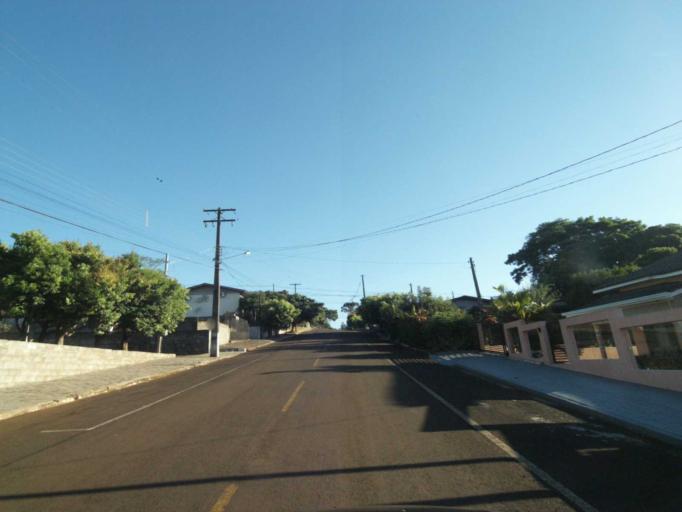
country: BR
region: Parana
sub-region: Coronel Vivida
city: Coronel Vivida
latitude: -25.9669
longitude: -52.8124
